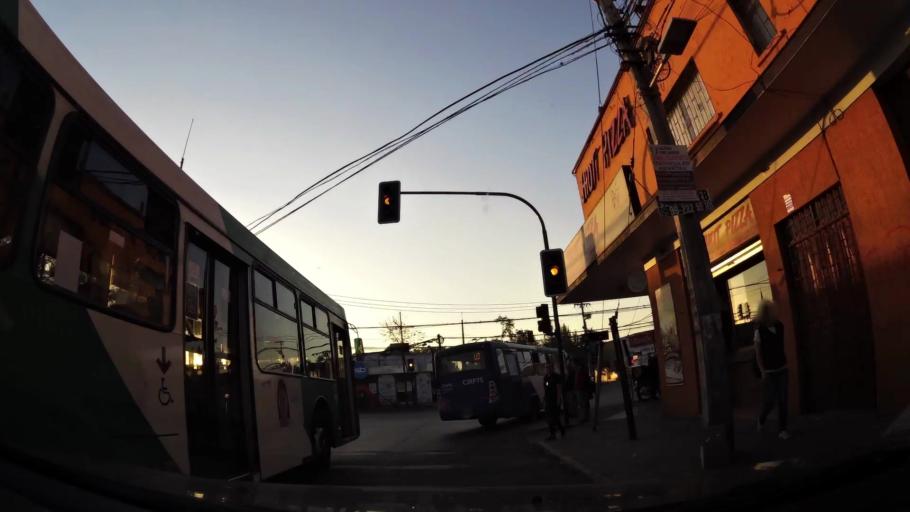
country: CL
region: Santiago Metropolitan
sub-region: Provincia de Santiago
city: La Pintana
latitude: -33.5457
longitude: -70.6680
